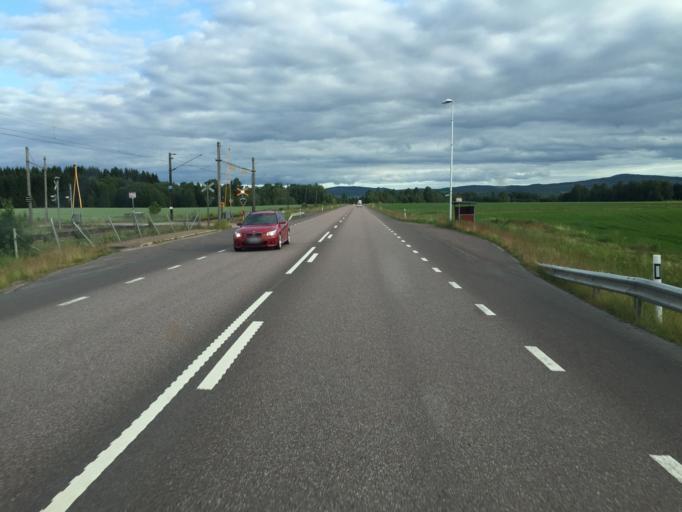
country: SE
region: Dalarna
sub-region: Gagnefs Kommun
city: Djuras
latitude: 60.5753
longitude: 15.1230
